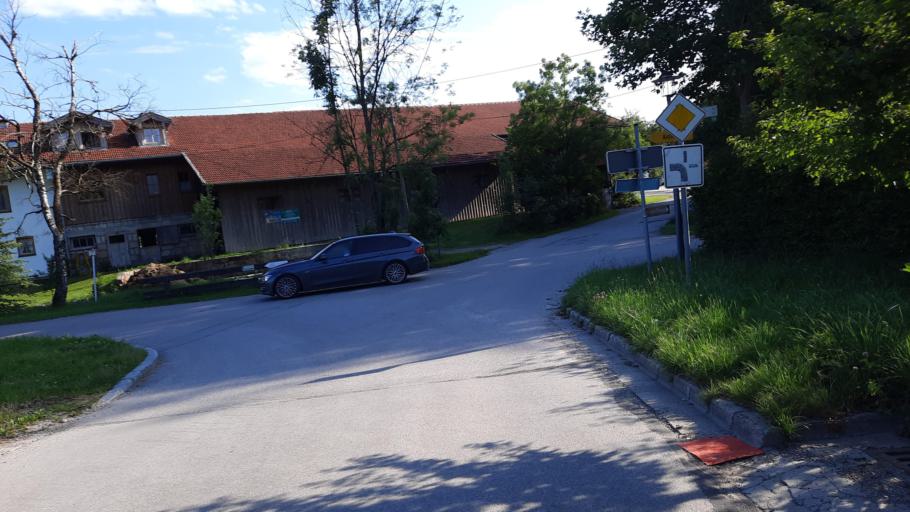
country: DE
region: Bavaria
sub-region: Upper Bavaria
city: Glonn
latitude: 47.9575
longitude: 11.8981
